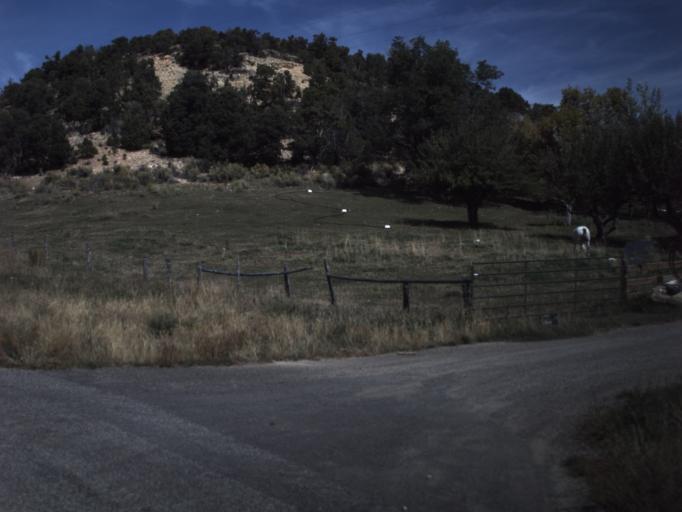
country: US
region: Utah
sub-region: Wayne County
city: Loa
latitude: 37.9396
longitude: -111.4323
